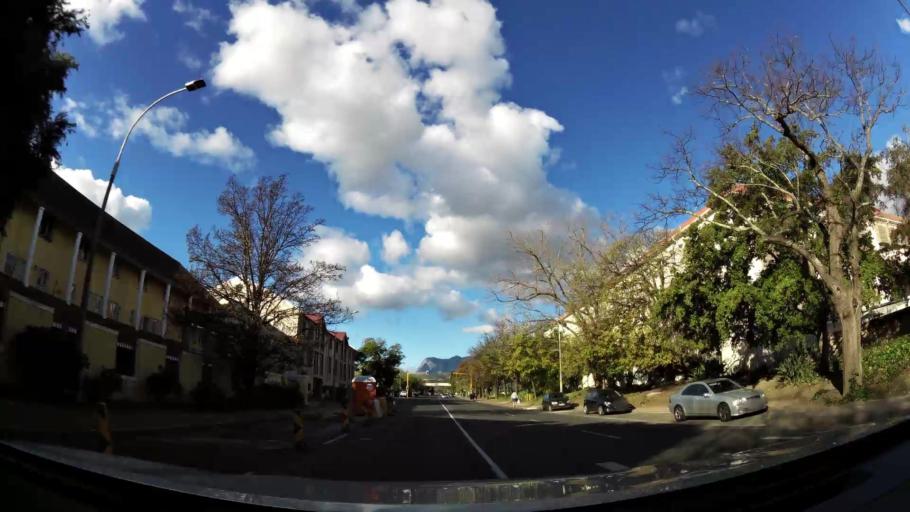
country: ZA
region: Western Cape
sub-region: Cape Winelands District Municipality
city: Stellenbosch
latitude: -33.9318
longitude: 18.8628
